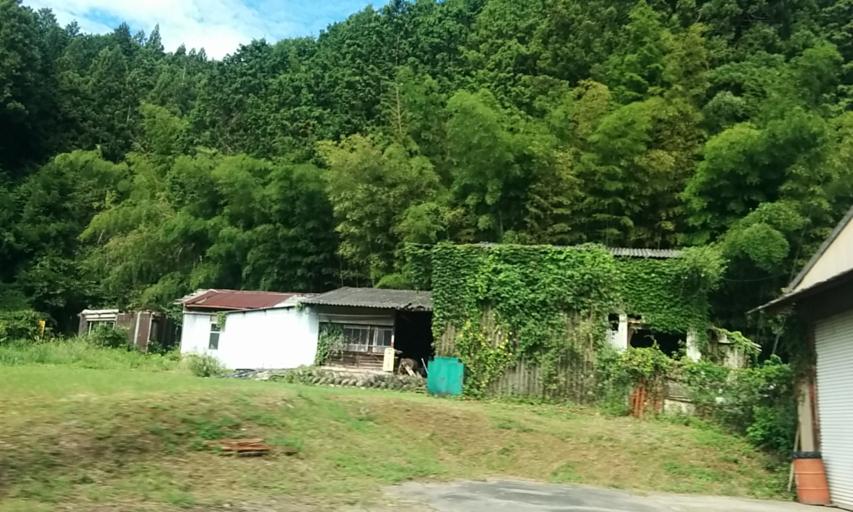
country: JP
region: Gifu
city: Minokamo
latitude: 35.5854
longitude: 137.0844
